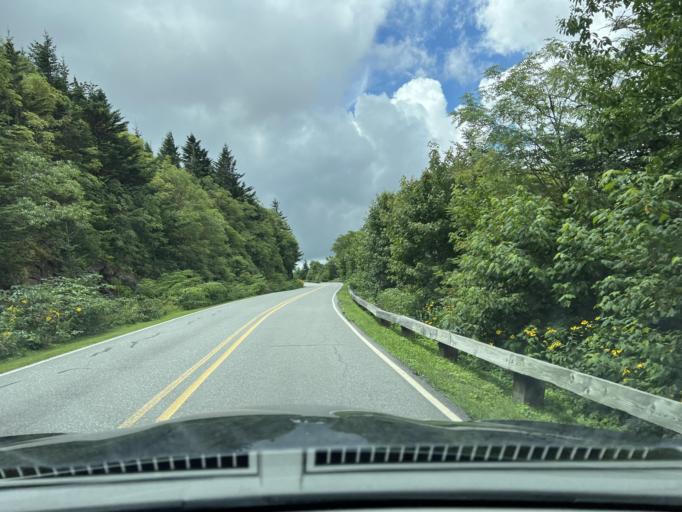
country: US
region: North Carolina
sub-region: Buncombe County
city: Black Mountain
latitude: 35.7503
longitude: -82.2759
